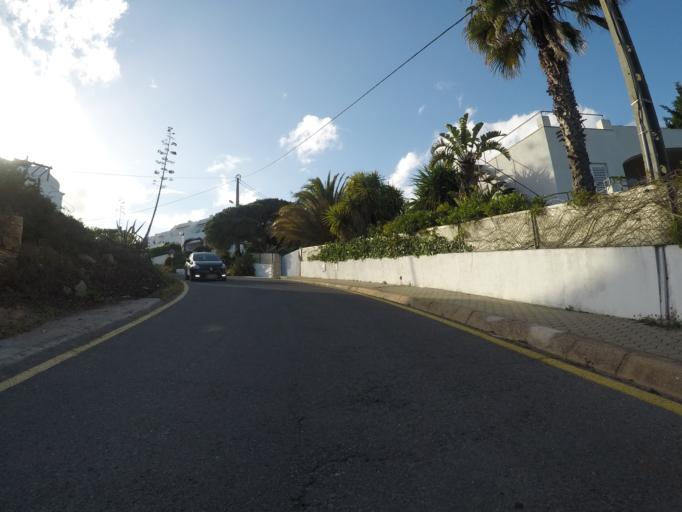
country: PT
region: Faro
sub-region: Lagoa
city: Carvoeiro
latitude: 37.0890
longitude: -8.4275
